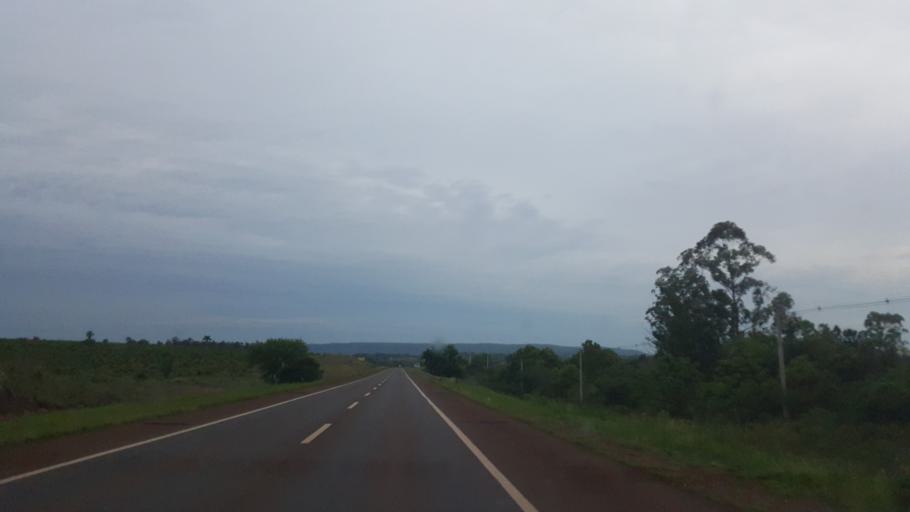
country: AR
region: Misiones
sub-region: Departamento de Apostoles
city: San Jose
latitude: -27.7736
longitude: -55.8074
